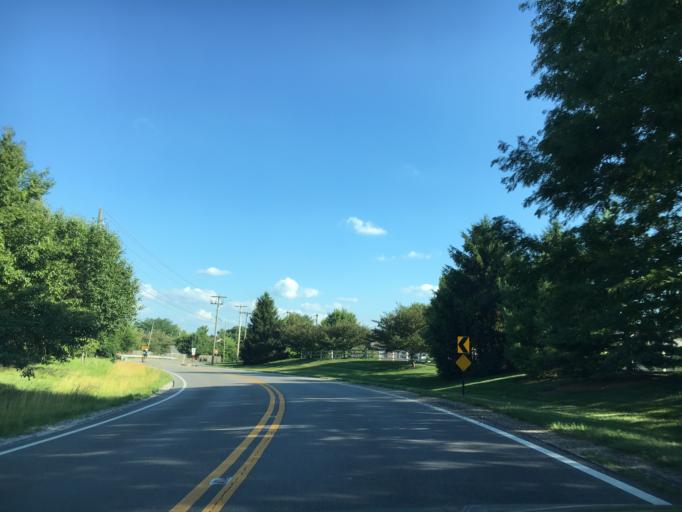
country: US
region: Ohio
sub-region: Franklin County
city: Hilliard
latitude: 40.0004
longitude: -83.1661
